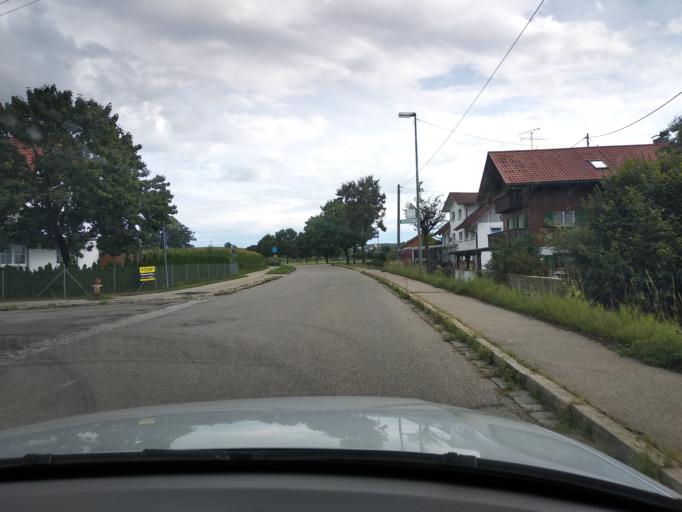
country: DE
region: Bavaria
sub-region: Swabia
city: Woringen
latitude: 47.8971
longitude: 10.2071
